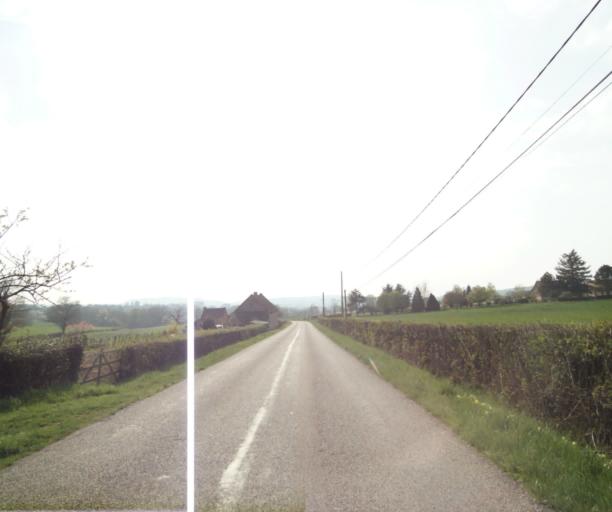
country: FR
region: Bourgogne
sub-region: Departement de Saone-et-Loire
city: Matour
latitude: 46.4833
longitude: 4.4574
